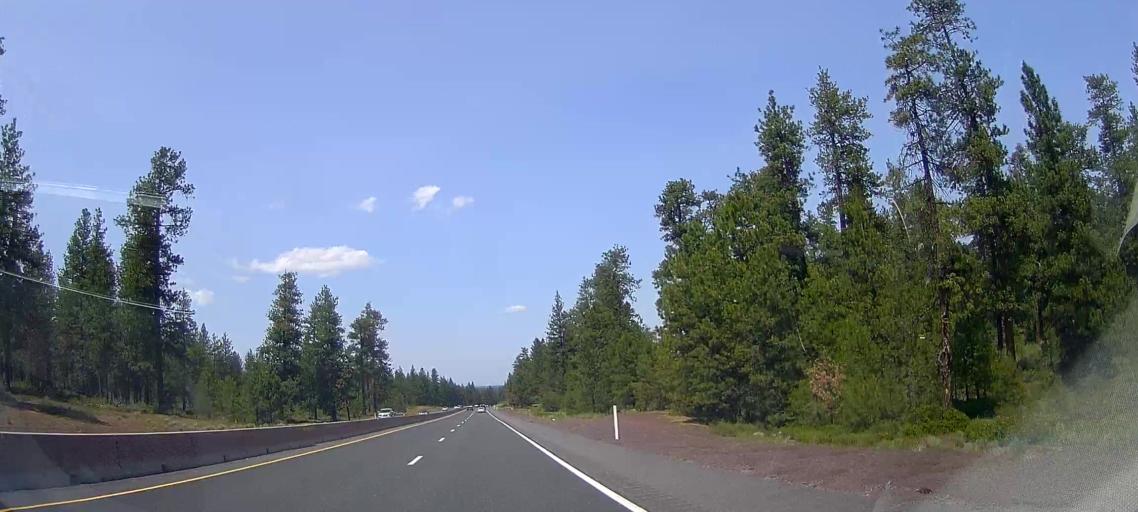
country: US
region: Oregon
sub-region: Deschutes County
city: Deschutes River Woods
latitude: 43.9210
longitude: -121.3503
